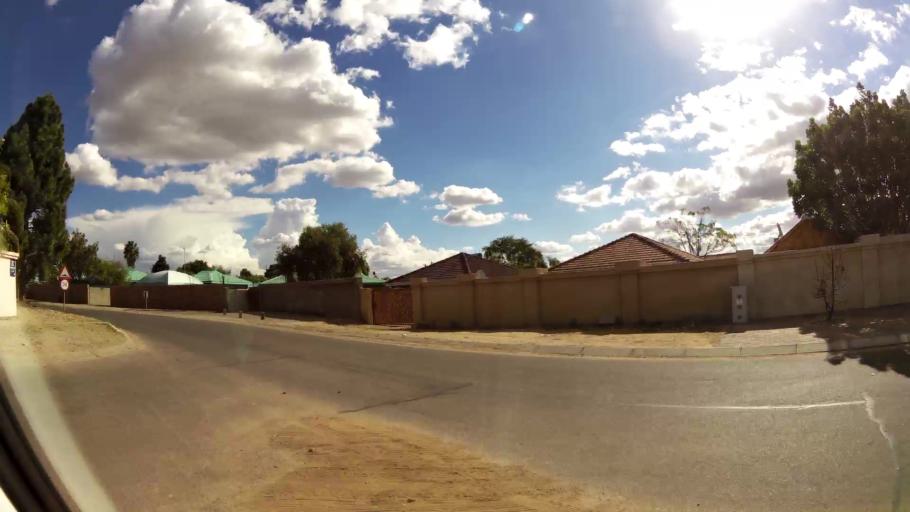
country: ZA
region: Limpopo
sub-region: Capricorn District Municipality
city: Polokwane
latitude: -23.8842
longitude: 29.4706
